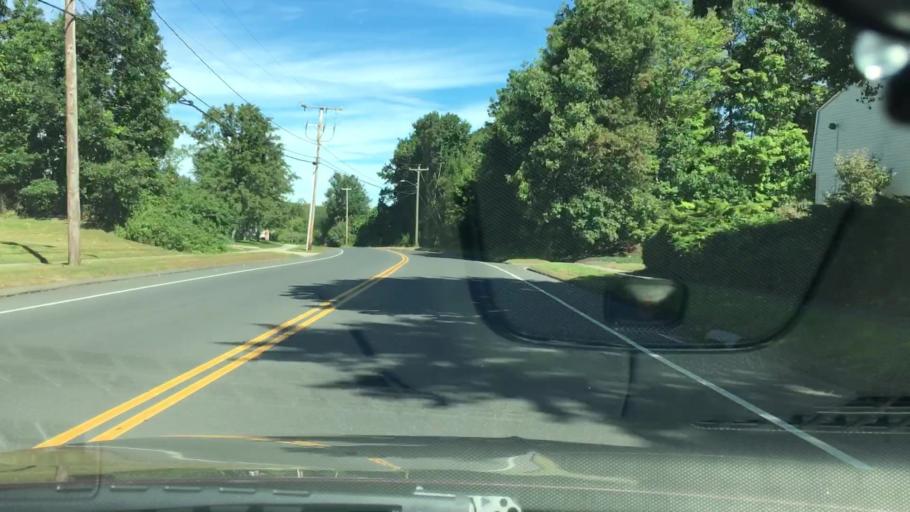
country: US
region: Connecticut
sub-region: Litchfield County
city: Terryville
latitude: 41.6862
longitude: -72.9840
